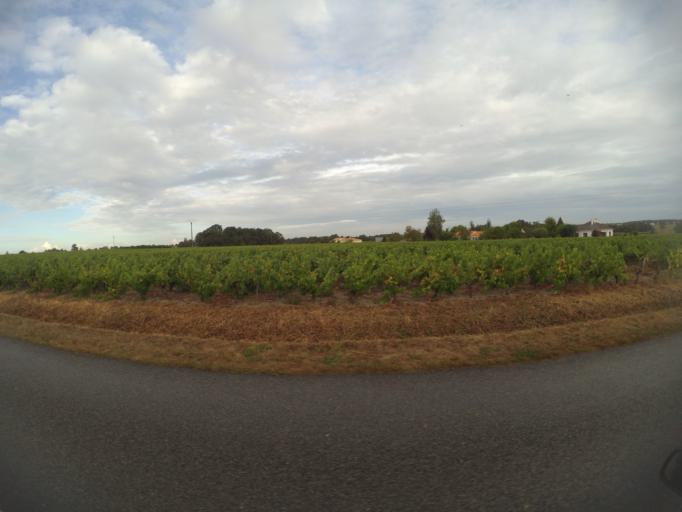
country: FR
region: Pays de la Loire
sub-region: Departement de la Loire-Atlantique
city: Aigrefeuille-sur-Maine
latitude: 47.0611
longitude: -1.4103
